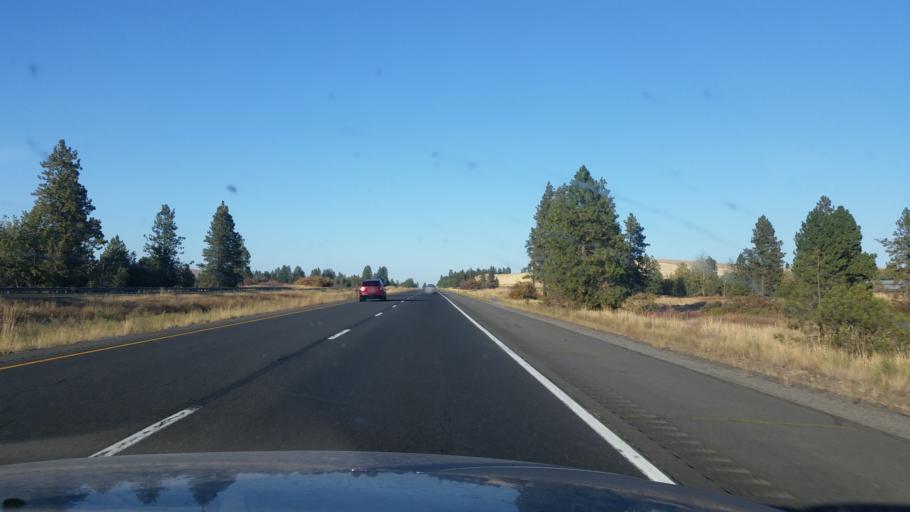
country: US
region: Washington
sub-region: Spokane County
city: Medical Lake
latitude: 47.5367
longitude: -117.6430
